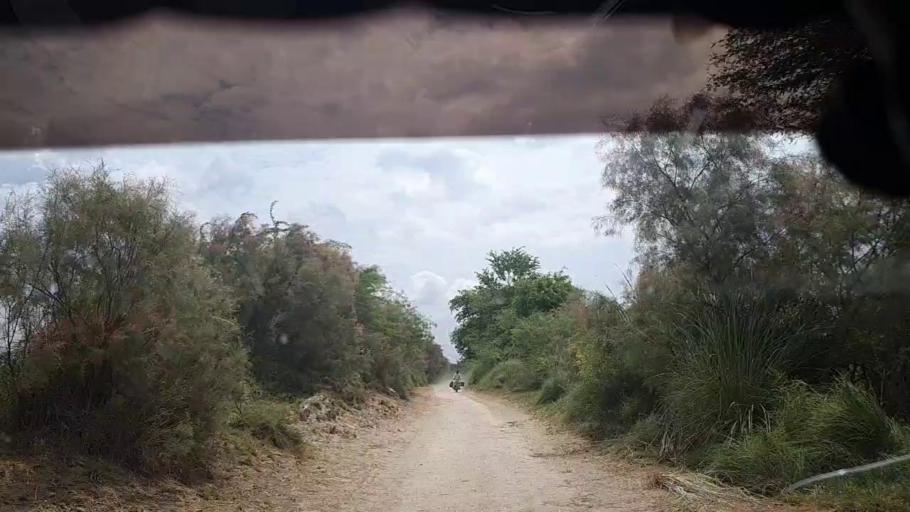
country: PK
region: Sindh
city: Rustam jo Goth
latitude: 28.0439
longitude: 68.9419
